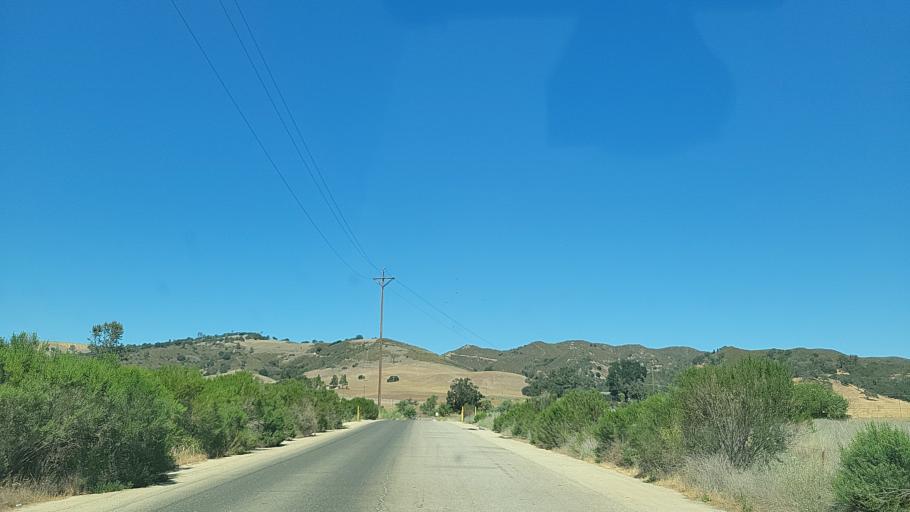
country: US
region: California
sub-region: San Luis Obispo County
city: Atascadero
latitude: 35.4606
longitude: -120.6268
